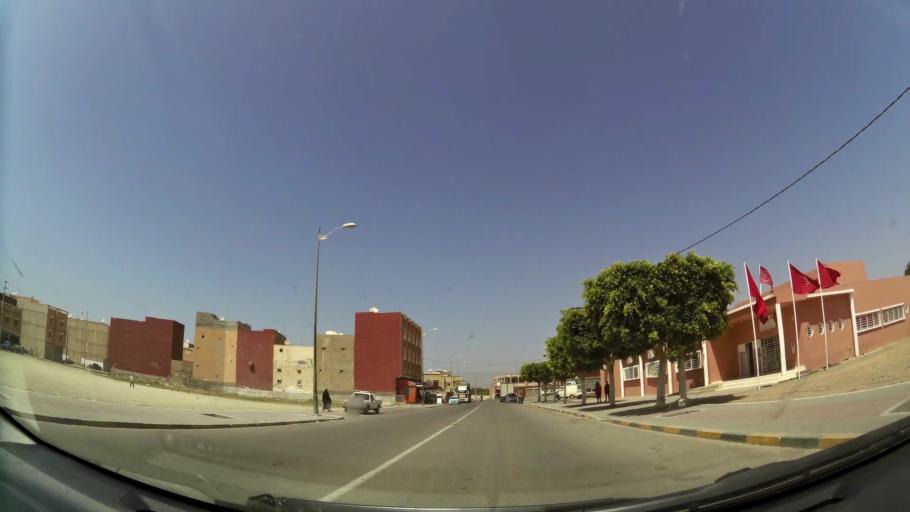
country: MA
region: Souss-Massa-Draa
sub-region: Inezgane-Ait Mellou
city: Inezgane
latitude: 30.3477
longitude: -9.5071
